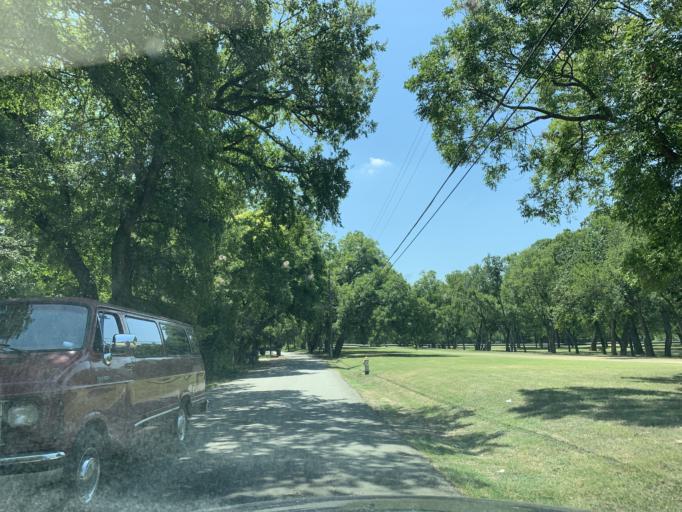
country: US
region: Texas
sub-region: Dallas County
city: Hutchins
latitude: 32.6836
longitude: -96.7952
